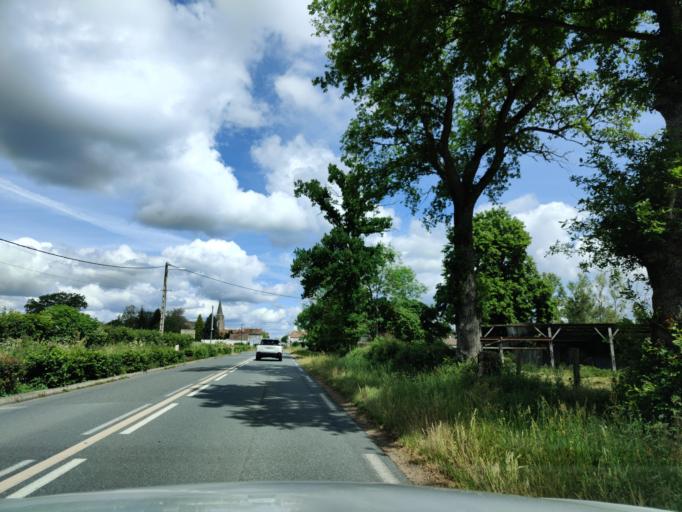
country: FR
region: Auvergne
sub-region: Departement de l'Allier
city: Durdat-Larequille
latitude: 46.2485
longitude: 2.7034
